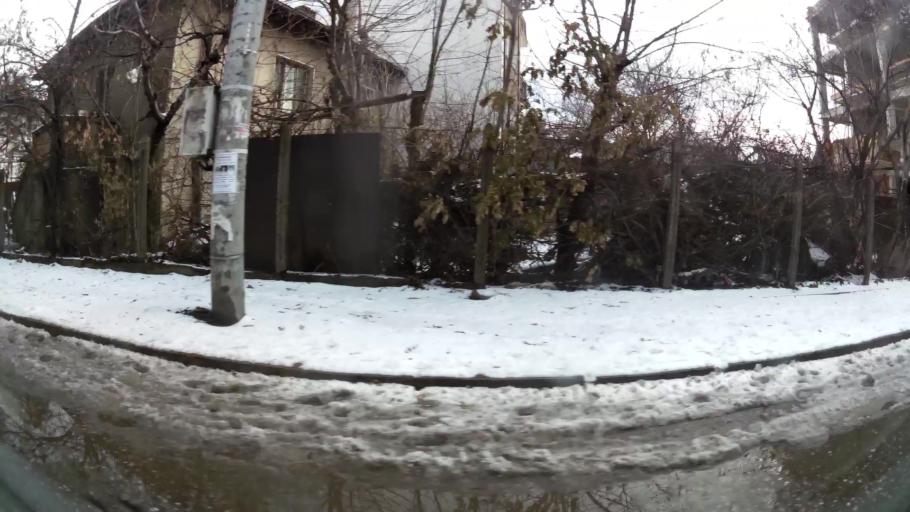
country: BG
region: Sofia-Capital
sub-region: Stolichna Obshtina
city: Sofia
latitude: 42.6987
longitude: 23.3667
